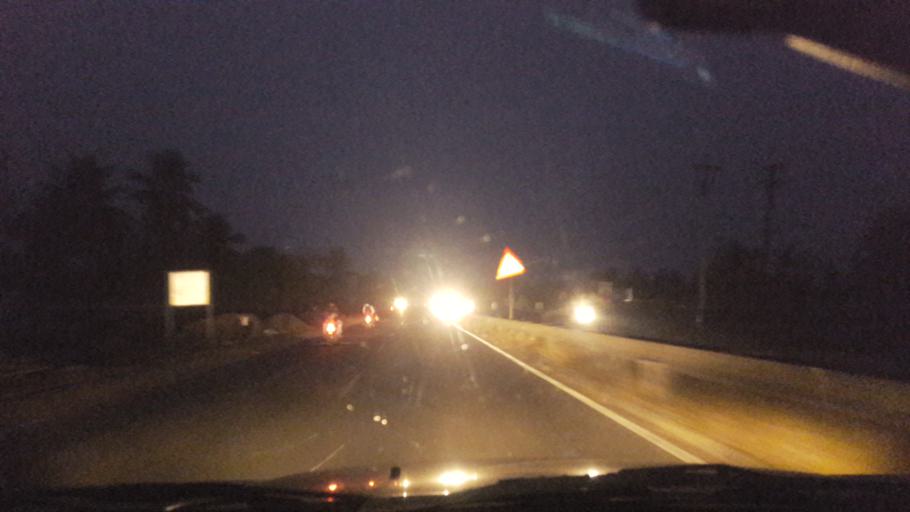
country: IN
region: Andhra Pradesh
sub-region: East Godavari
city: Peddapuram
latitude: 17.1344
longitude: 81.9544
